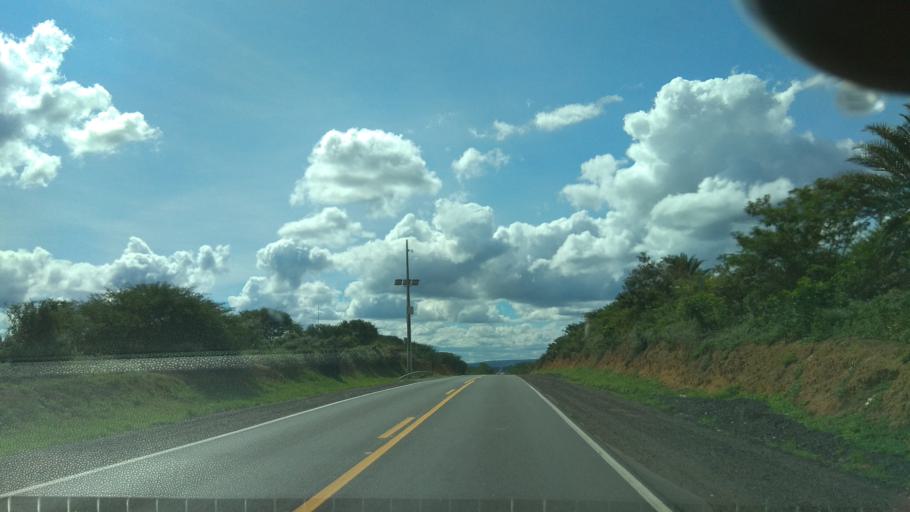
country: BR
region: Bahia
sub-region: Jaguaquara
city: Jaguaquara
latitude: -13.4327
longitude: -40.0288
